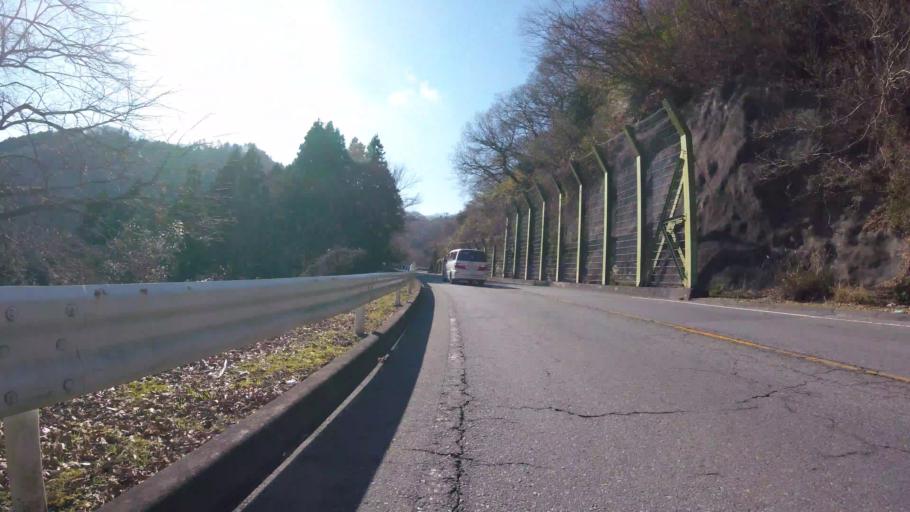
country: JP
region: Shizuoka
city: Ito
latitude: 34.9308
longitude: 139.0507
